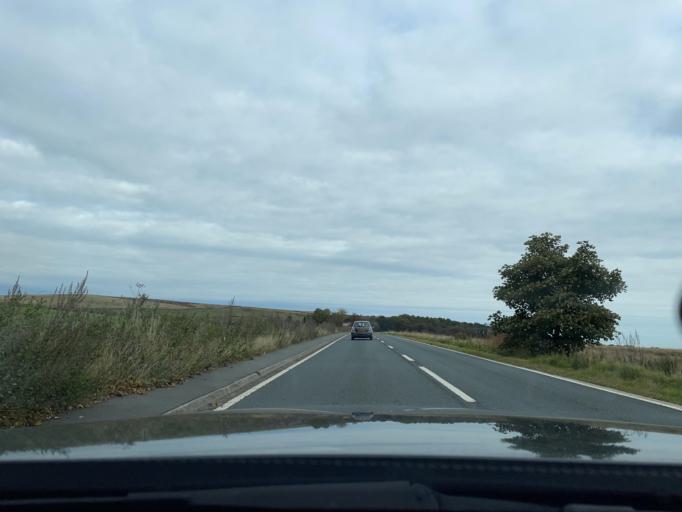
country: GB
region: England
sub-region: Derbyshire
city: Hathersage
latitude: 53.3878
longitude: -1.6529
